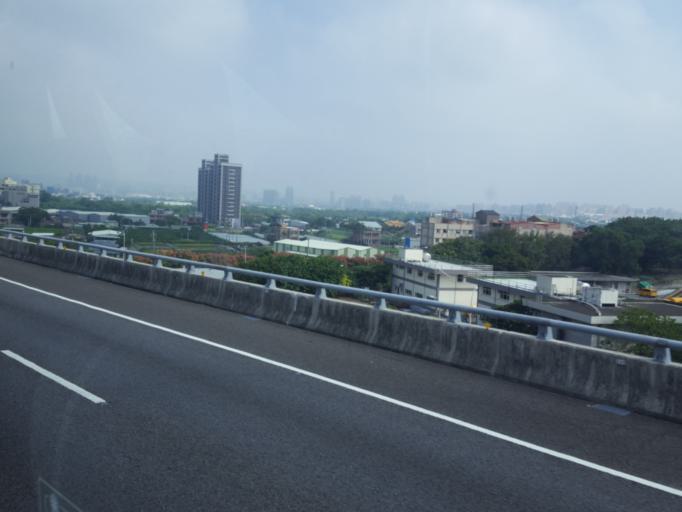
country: TW
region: Taiwan
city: Taoyuan City
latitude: 25.0021
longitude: 121.2530
